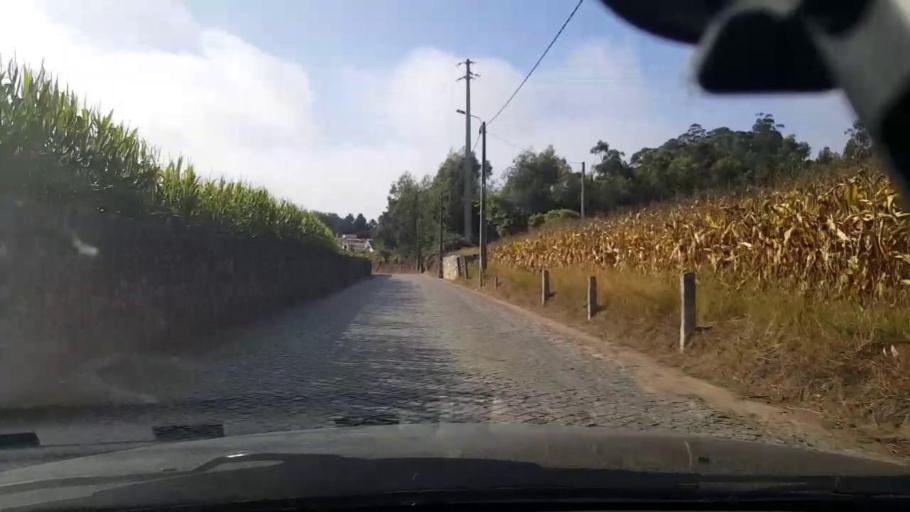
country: PT
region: Porto
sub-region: Maia
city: Gemunde
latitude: 41.2688
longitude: -8.6761
